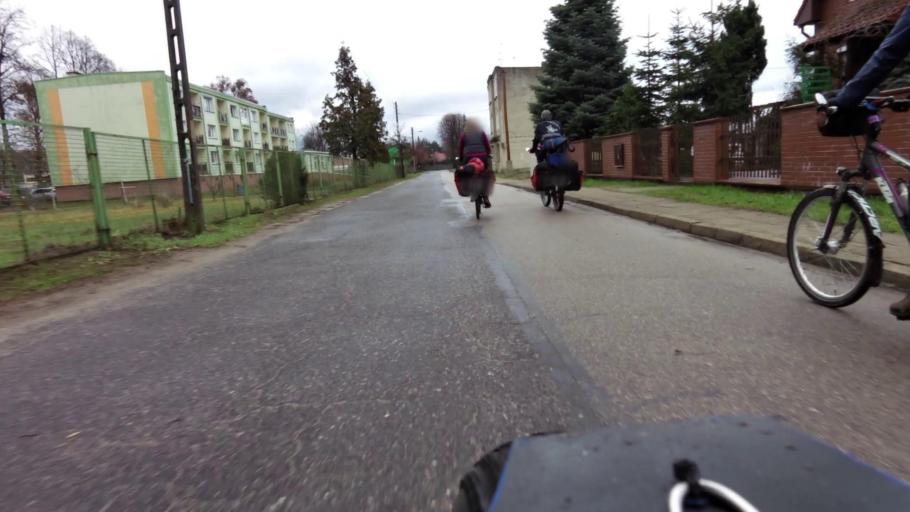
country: PL
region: Lubusz
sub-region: Powiat gorzowski
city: Witnica
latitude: 52.6847
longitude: 14.8860
